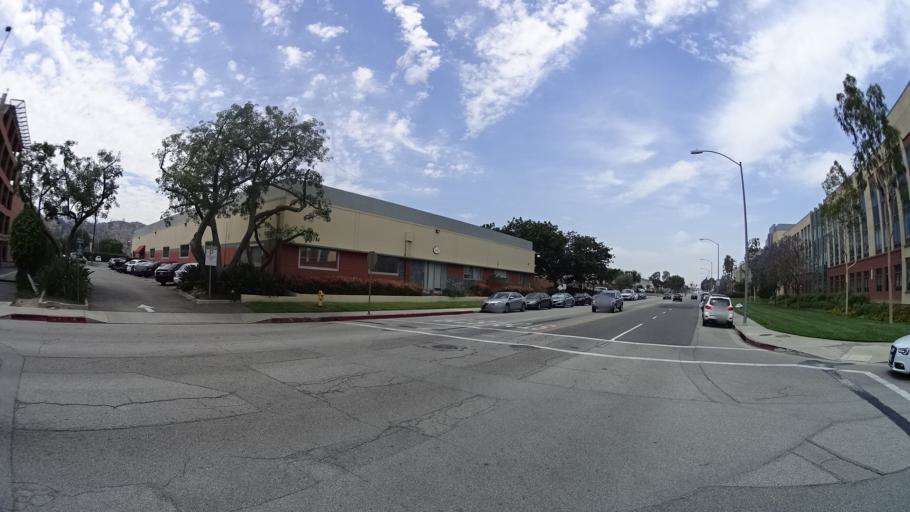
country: US
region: California
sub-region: Los Angeles County
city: North Glendale
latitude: 34.1588
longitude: -118.2856
